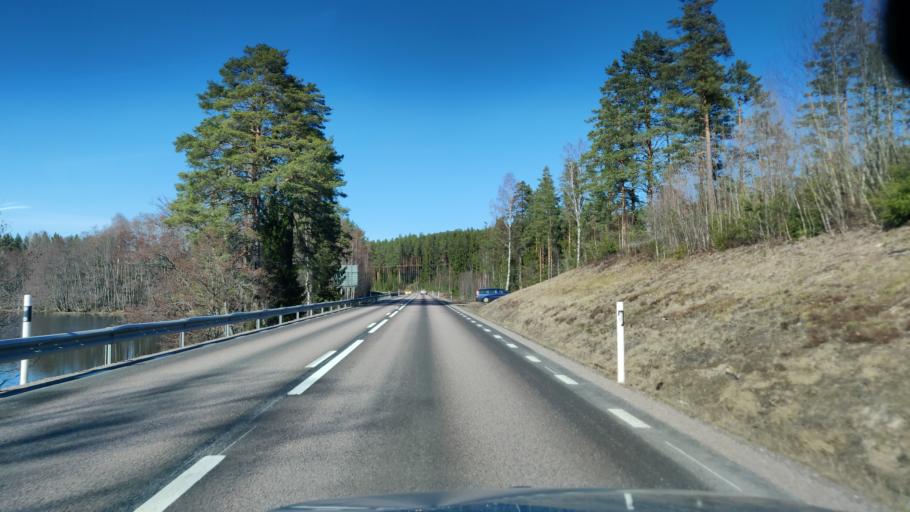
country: SE
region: Vaermland
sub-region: Hagfors Kommun
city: Hagfors
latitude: 59.9219
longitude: 13.6735
